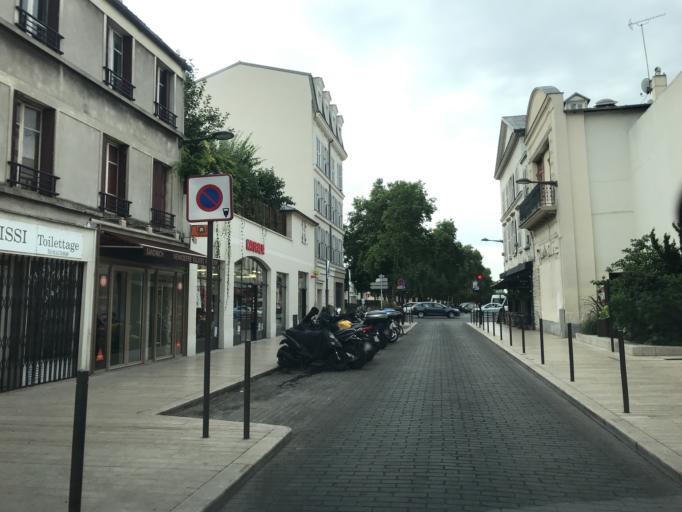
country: FR
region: Ile-de-France
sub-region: Departement du Val-de-Marne
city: Vincennes
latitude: 48.8455
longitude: 2.4346
